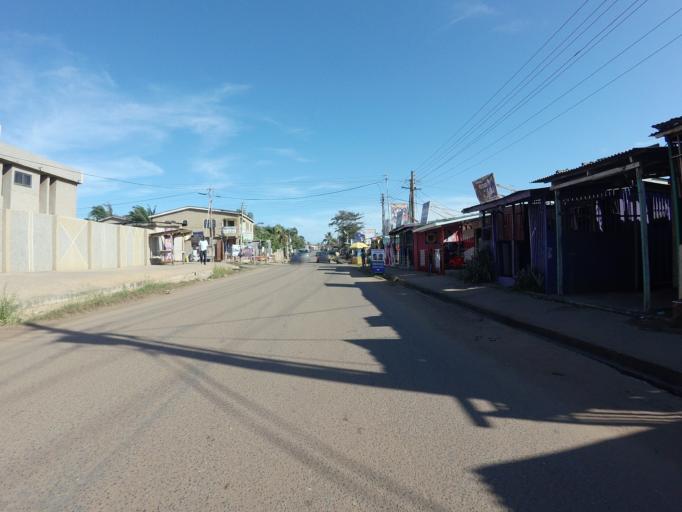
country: GH
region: Greater Accra
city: Nungua
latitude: 5.5926
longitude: -0.0836
